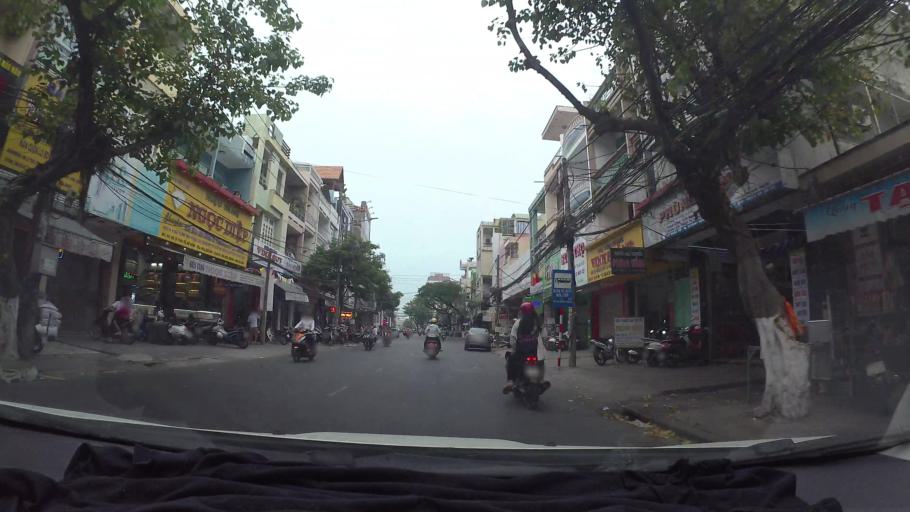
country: VN
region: Da Nang
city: Da Nang
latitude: 16.0661
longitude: 108.2081
